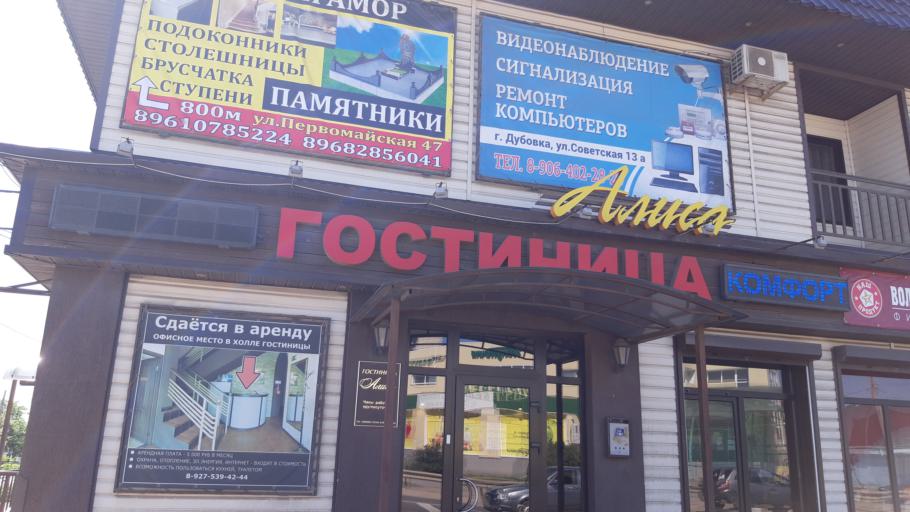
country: RU
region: Volgograd
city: Dubovka
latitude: 49.0599
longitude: 44.8221
